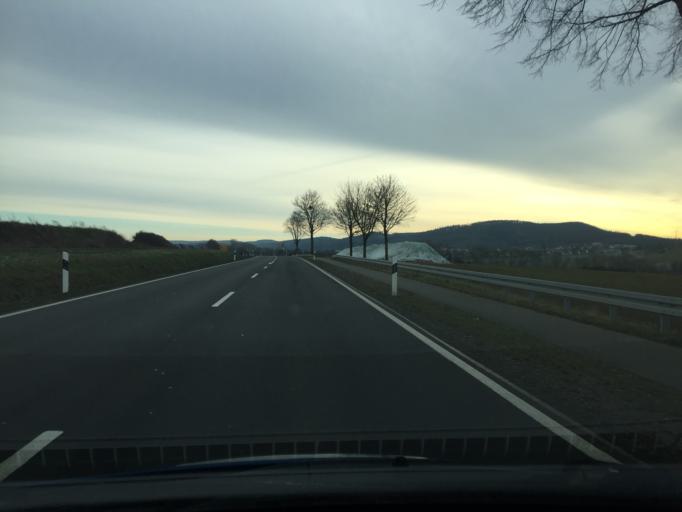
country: DE
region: Lower Saxony
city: Luerdissen
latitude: 51.9462
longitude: 9.6252
